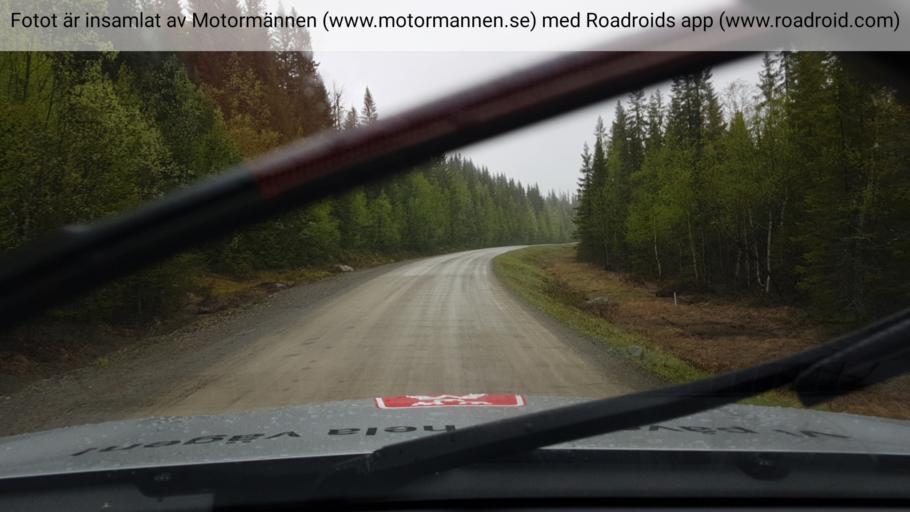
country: SE
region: Jaemtland
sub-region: Krokoms Kommun
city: Valla
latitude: 63.0436
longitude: 13.9606
